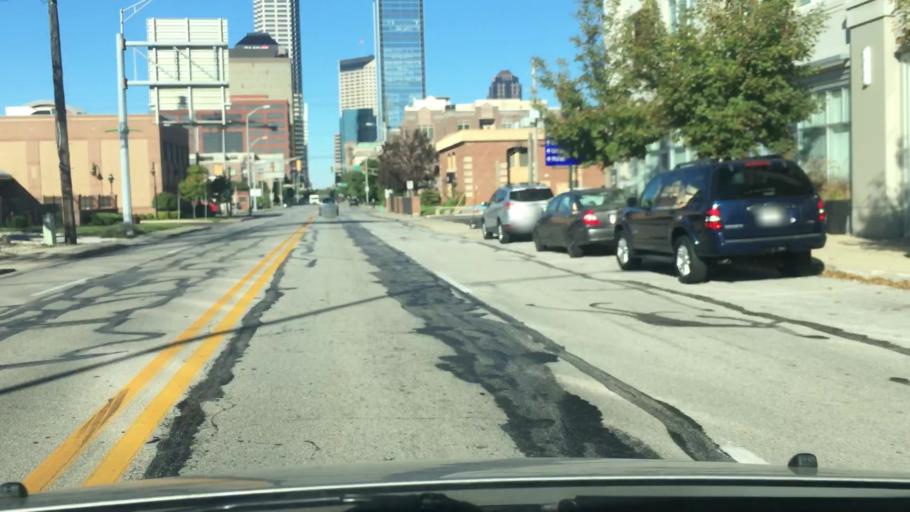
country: US
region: Indiana
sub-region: Marion County
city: Indianapolis
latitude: 39.7697
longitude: -86.1477
